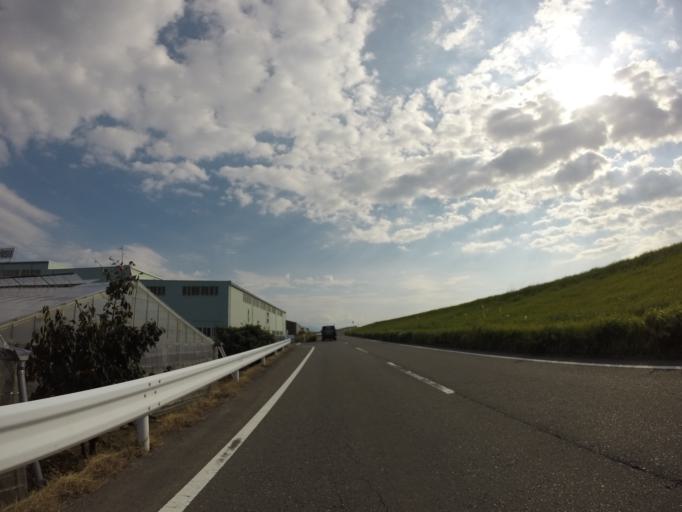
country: JP
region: Shizuoka
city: Fuji
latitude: 35.1378
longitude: 138.6380
